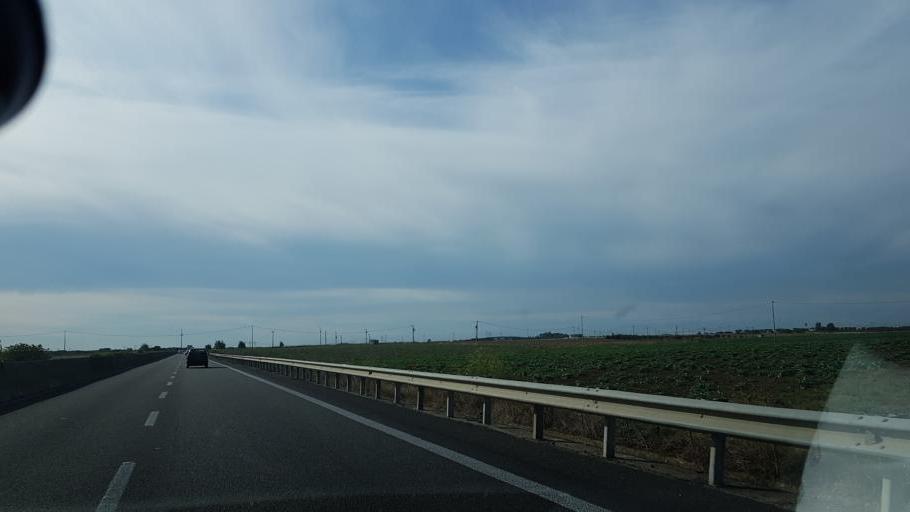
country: IT
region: Apulia
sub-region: Provincia di Brindisi
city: La Rosa
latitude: 40.5904
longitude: 17.9729
